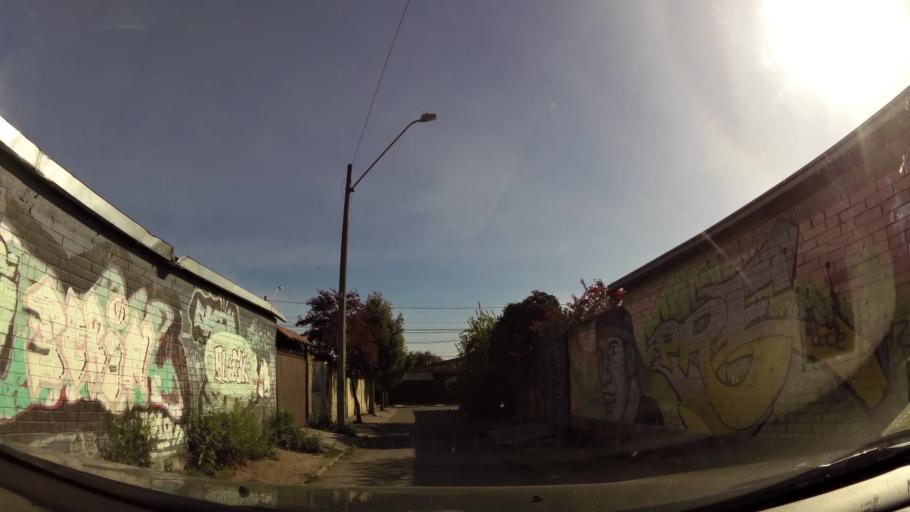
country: CL
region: Santiago Metropolitan
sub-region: Provincia de Cordillera
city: Puente Alto
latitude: -33.6063
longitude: -70.5984
